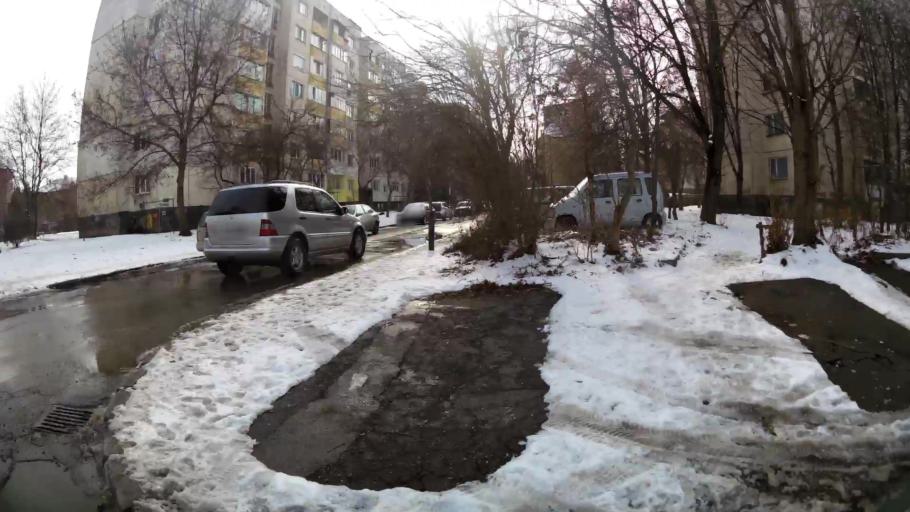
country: BG
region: Sofia-Capital
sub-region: Stolichna Obshtina
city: Sofia
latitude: 42.7055
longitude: 23.3538
